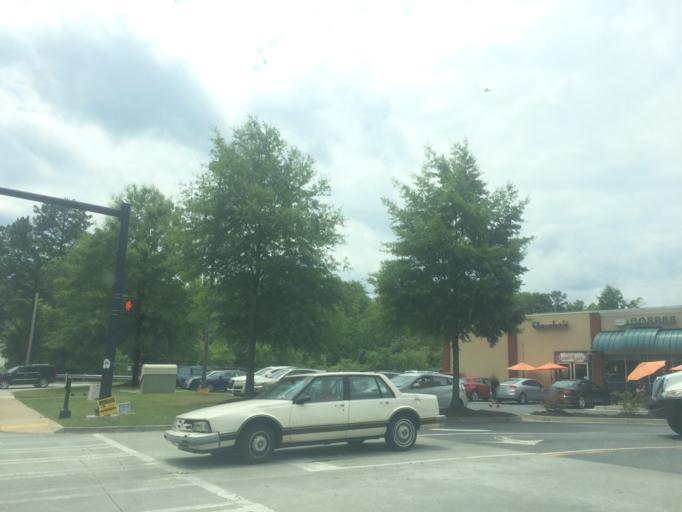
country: US
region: Georgia
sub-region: DeKalb County
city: Chamblee
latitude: 33.8626
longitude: -84.2873
